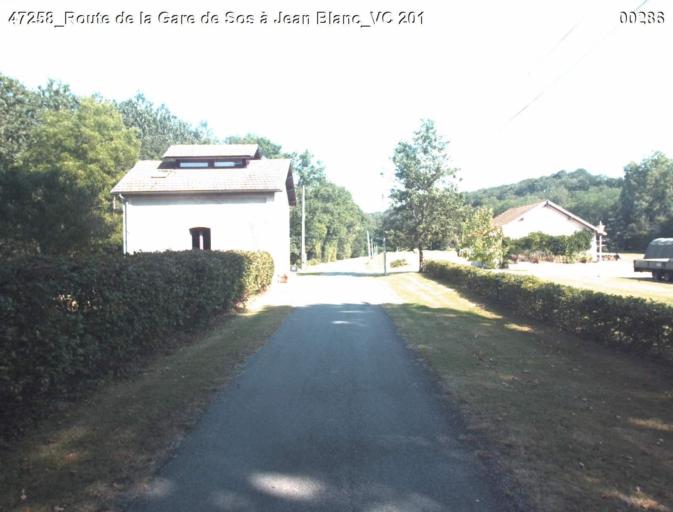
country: FR
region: Midi-Pyrenees
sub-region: Departement du Gers
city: Montreal
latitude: 44.0386
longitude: 0.1466
